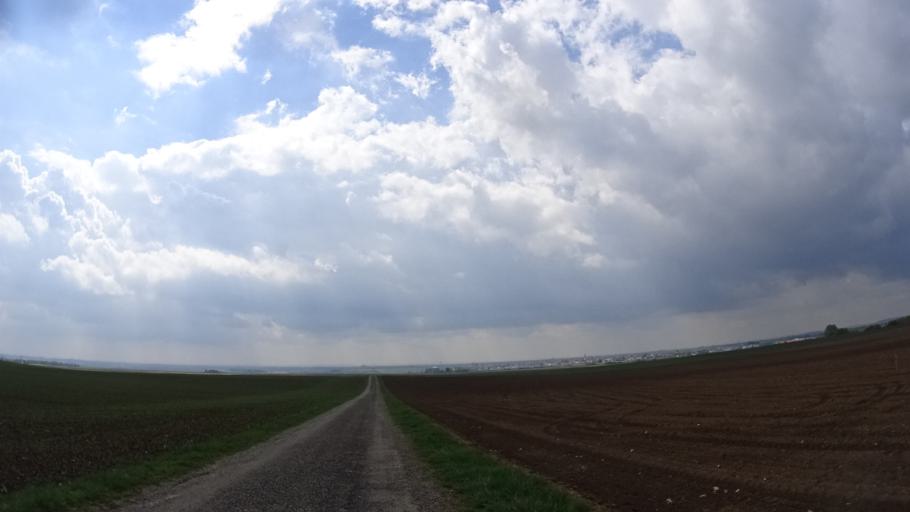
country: DE
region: Bavaria
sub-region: Upper Bavaria
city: Hitzhofen
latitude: 48.8407
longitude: 11.3298
